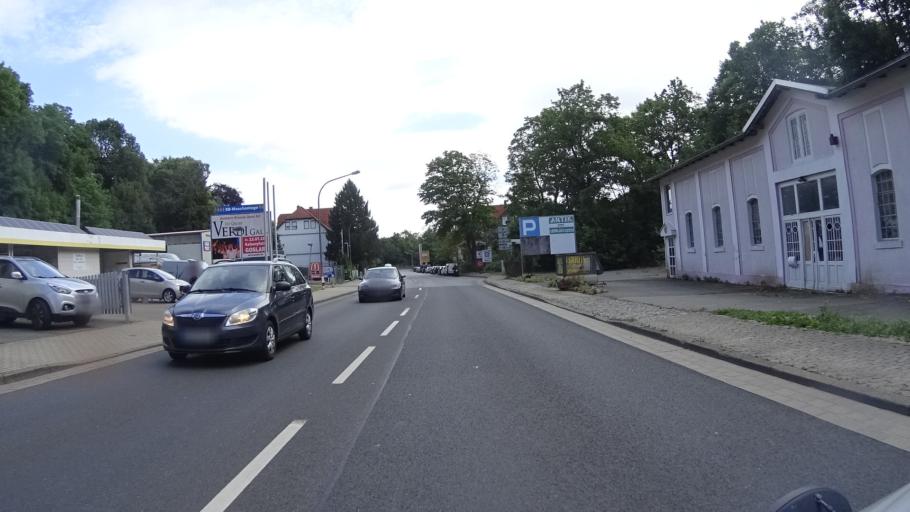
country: DE
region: Lower Saxony
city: Goslar
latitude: 51.9004
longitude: 10.4158
